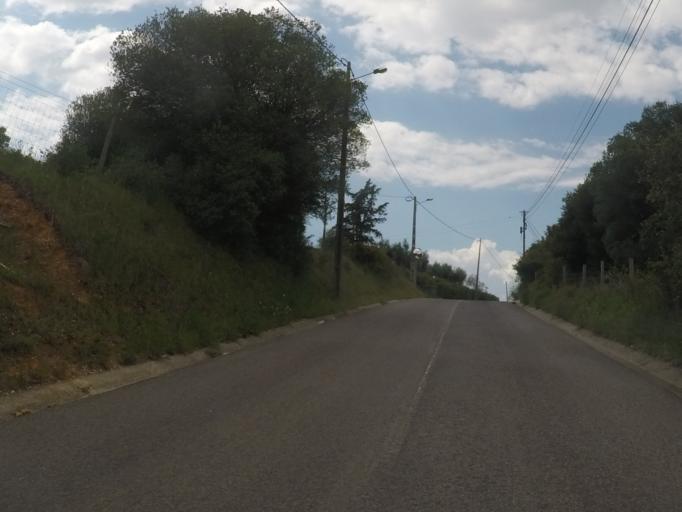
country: PT
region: Setubal
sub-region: Palmela
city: Quinta do Anjo
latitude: 38.5106
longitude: -9.0048
